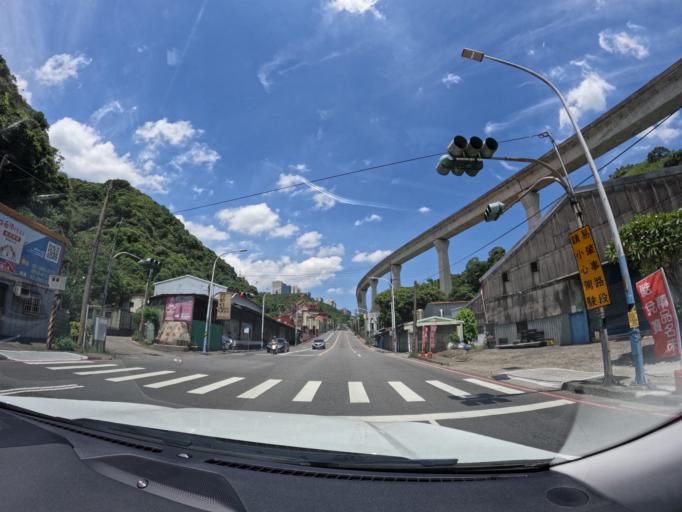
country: TW
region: Taipei
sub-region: Taipei
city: Banqiao
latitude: 25.0301
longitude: 121.4009
